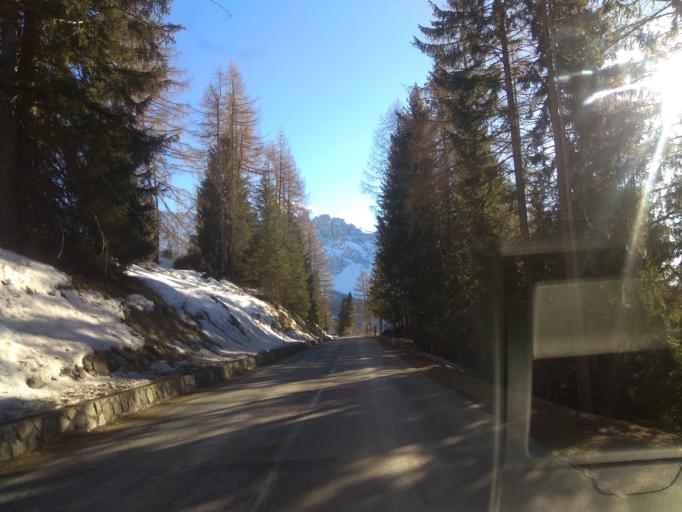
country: IT
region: Trentino-Alto Adige
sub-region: Bolzano
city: Nova Levante
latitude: 46.4252
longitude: 11.5969
